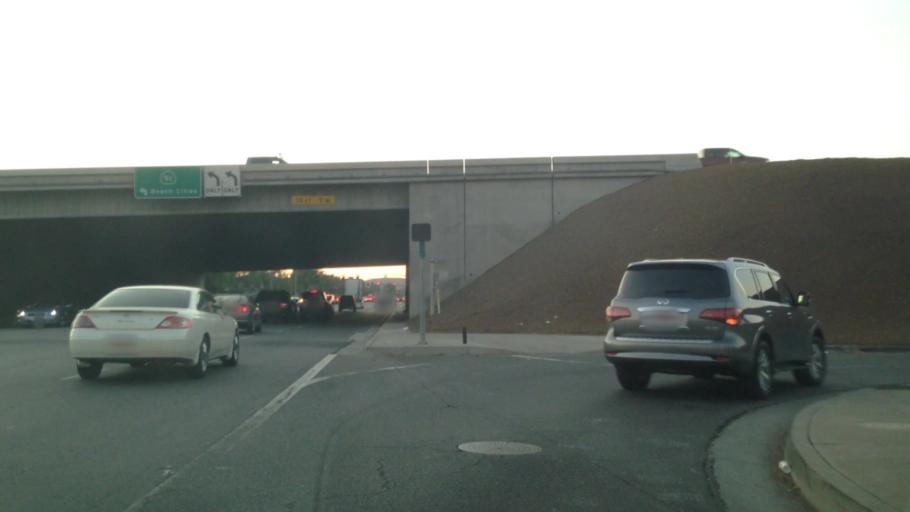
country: US
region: California
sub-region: Riverside County
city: Home Gardens
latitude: 33.8857
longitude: -117.5173
